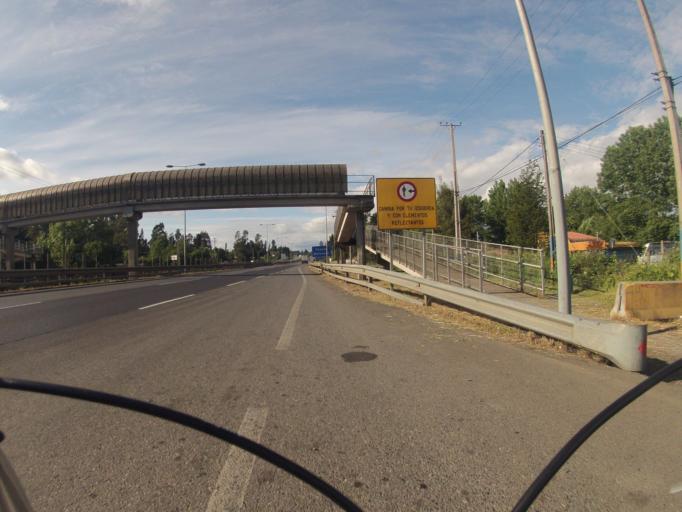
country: CL
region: Araucania
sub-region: Provincia de Cautin
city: Temuco
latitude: -38.8274
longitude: -72.6235
